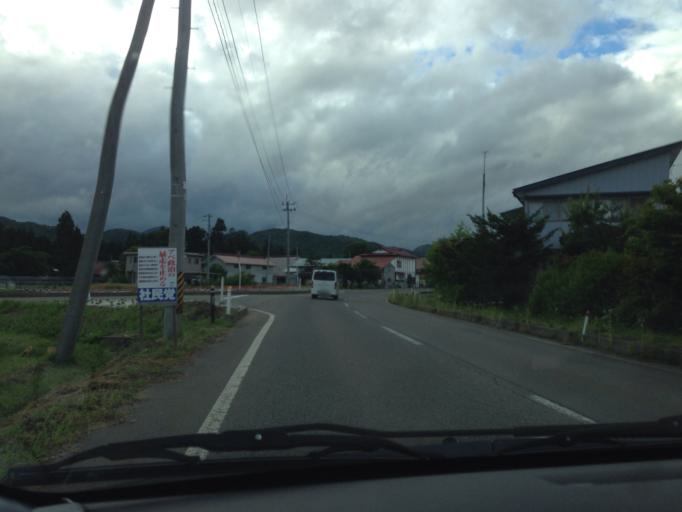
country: JP
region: Fukushima
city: Kitakata
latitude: 37.7063
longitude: 139.8562
